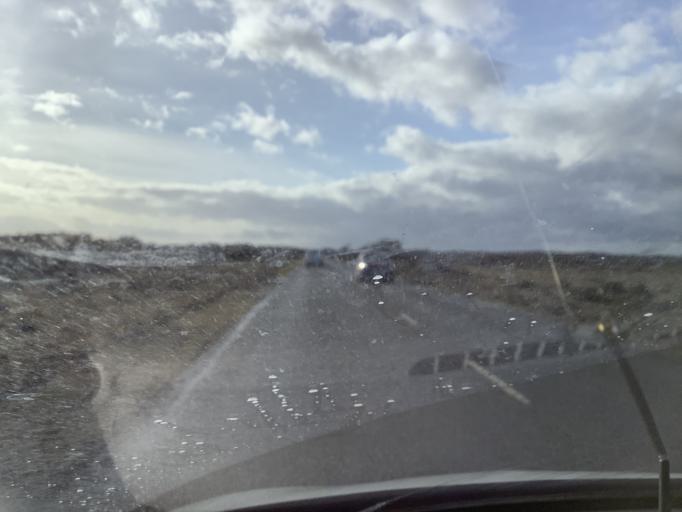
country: GB
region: England
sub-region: Hampshire
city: Hythe
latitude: 50.8266
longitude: -1.4109
